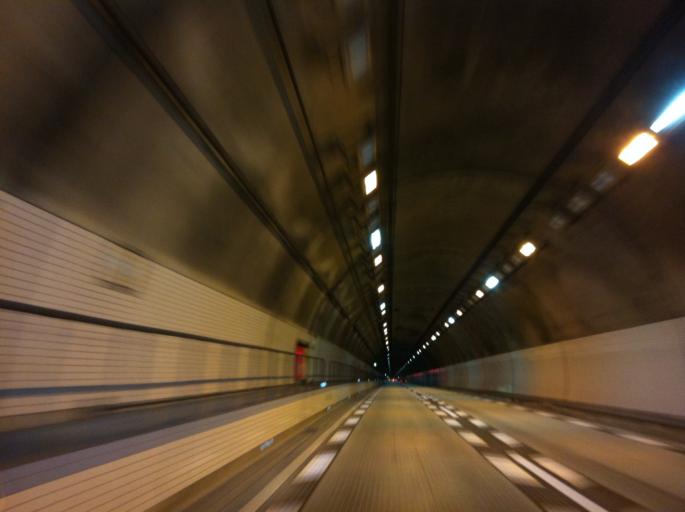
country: JP
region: Shizuoka
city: Yaizu
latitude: 34.8981
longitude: 138.3359
